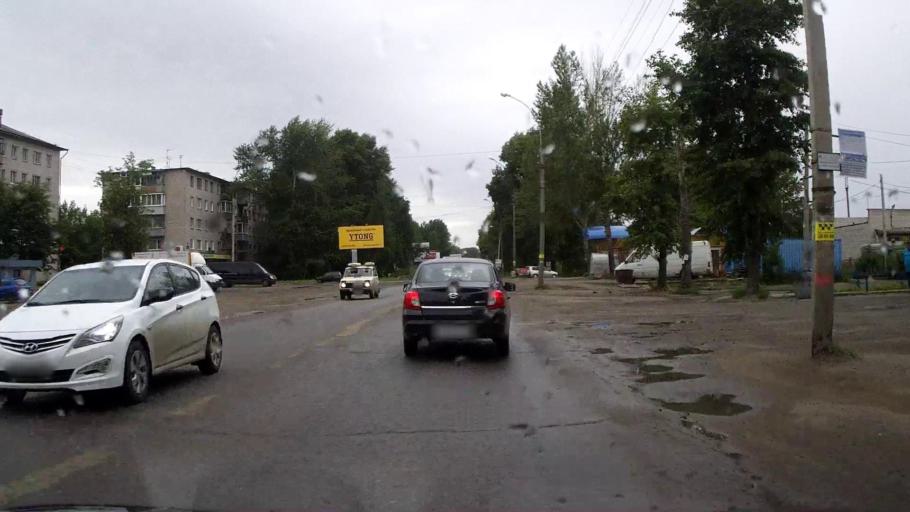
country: RU
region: Vologda
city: Vologda
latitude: 59.2062
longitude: 39.8630
